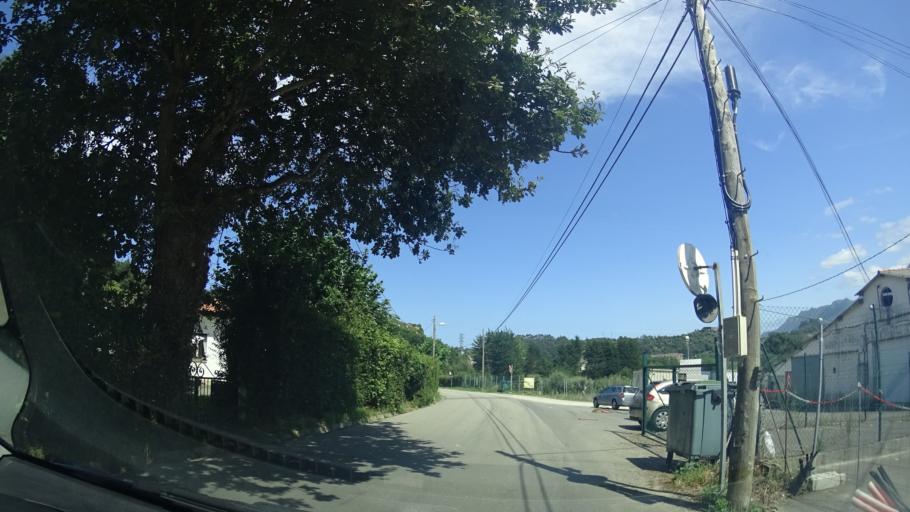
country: ES
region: Asturias
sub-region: Province of Asturias
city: Ribadesella
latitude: 43.4556
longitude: -5.0721
